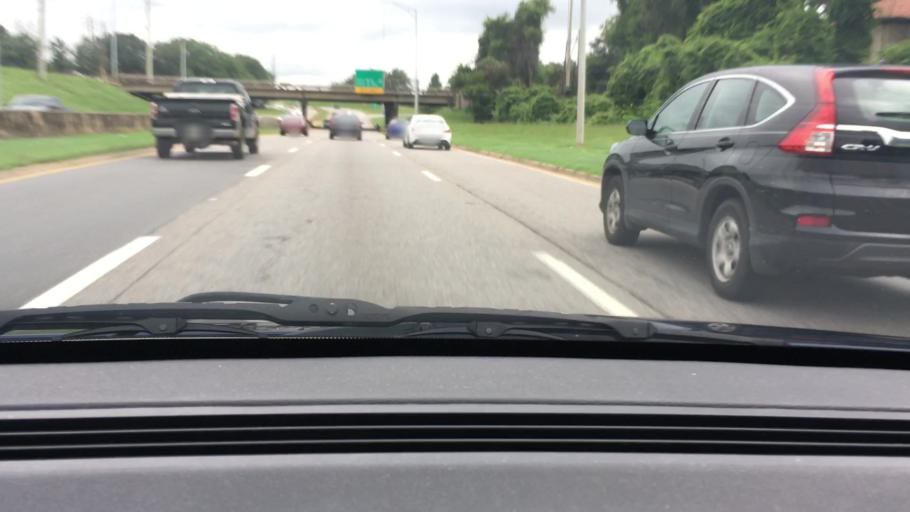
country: US
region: Alabama
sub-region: Tuscaloosa County
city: Tuscaloosa
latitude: 33.2047
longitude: -87.5247
